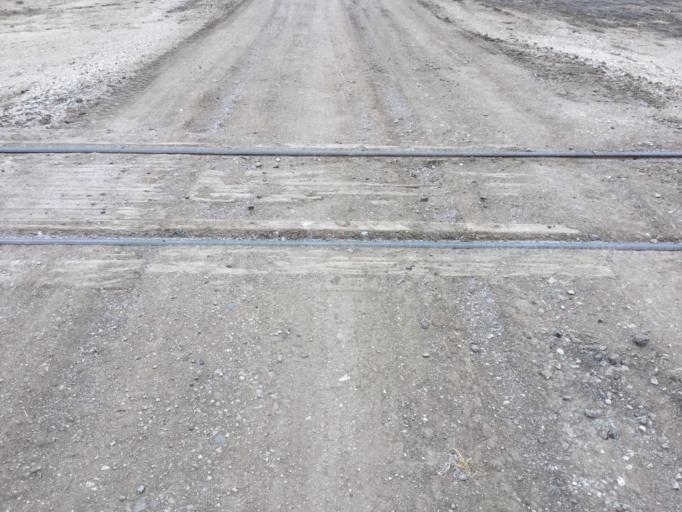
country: US
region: Kansas
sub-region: Scott County
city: Scott City
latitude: 38.4855
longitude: -100.7416
